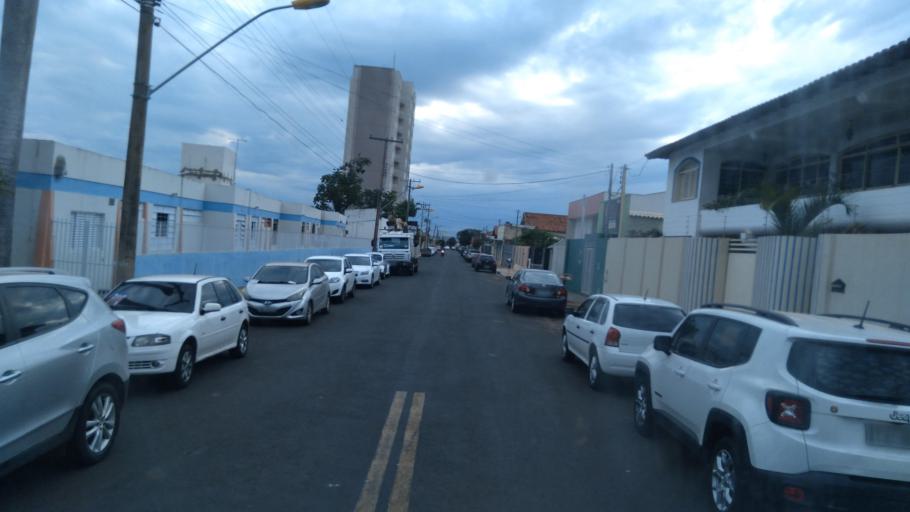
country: BR
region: Goias
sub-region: Mineiros
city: Mineiros
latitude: -17.5686
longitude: -52.5570
